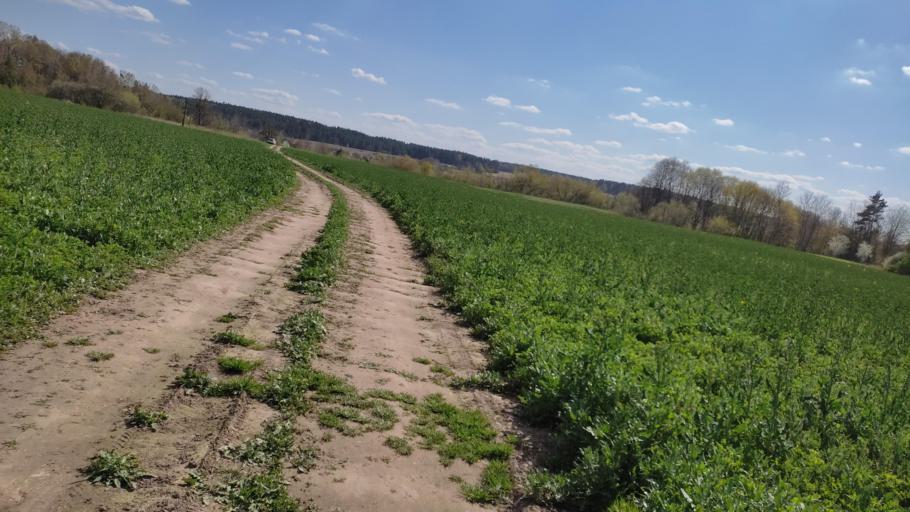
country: BY
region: Grodnenskaya
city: Hrodna
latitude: 53.6561
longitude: 23.9057
